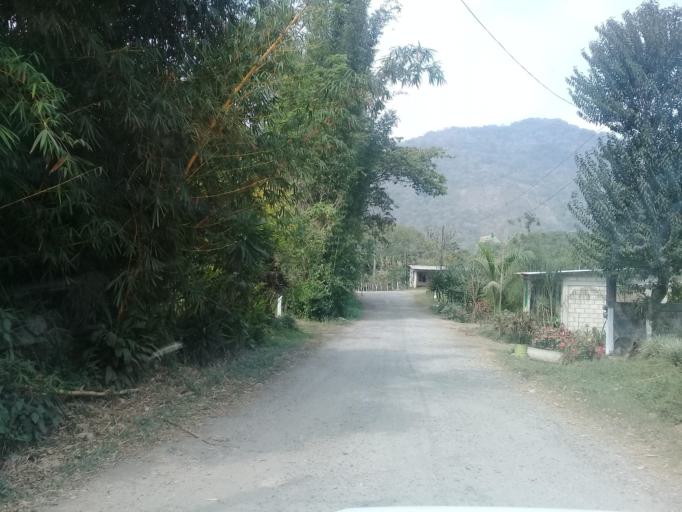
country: MX
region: Veracruz
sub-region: Ixtaczoquitlan
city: Capoluca
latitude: 18.8116
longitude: -96.9865
